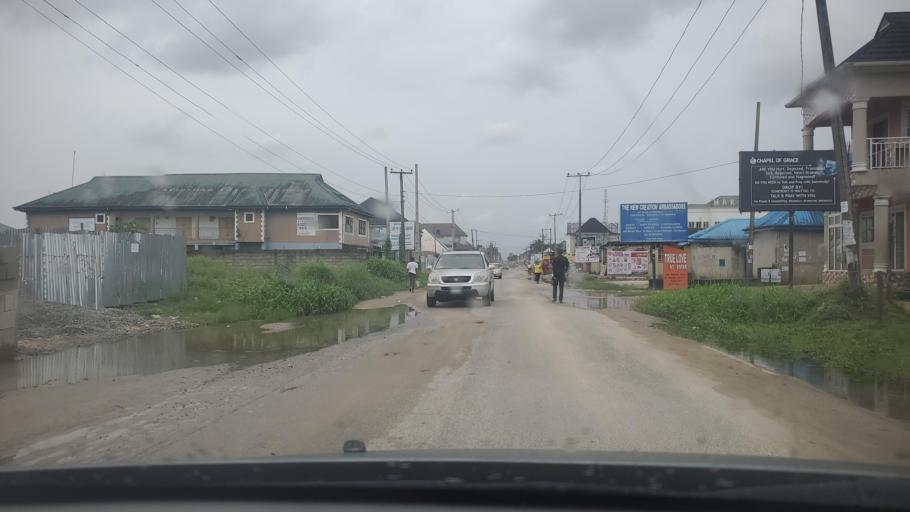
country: NG
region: Rivers
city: Port Harcourt
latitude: 4.8678
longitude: 6.9814
